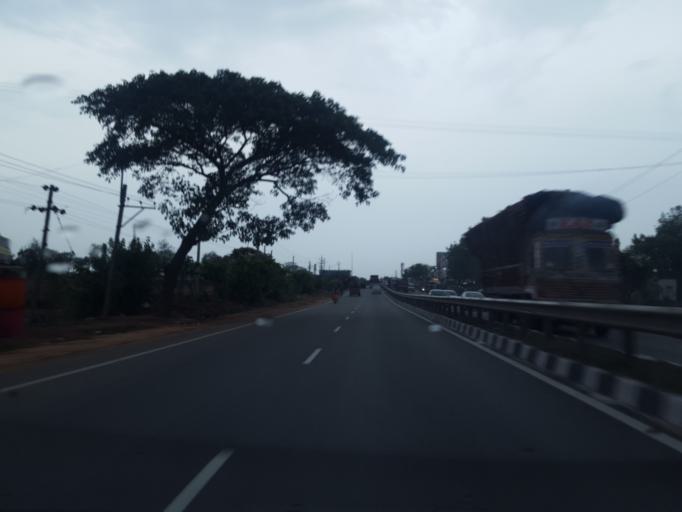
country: IN
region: Telangana
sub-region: Mahbubnagar
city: Farrukhnagar
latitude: 17.1546
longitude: 78.2924
